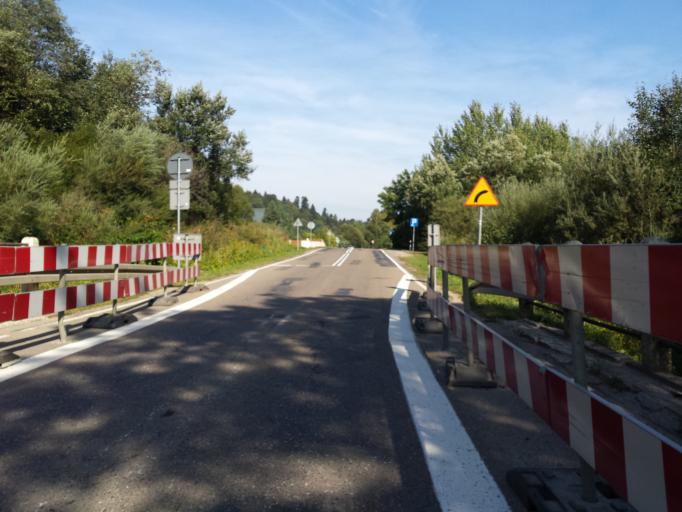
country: PL
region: Subcarpathian Voivodeship
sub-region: Powiat leski
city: Baligrod
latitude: 49.2747
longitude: 22.2861
